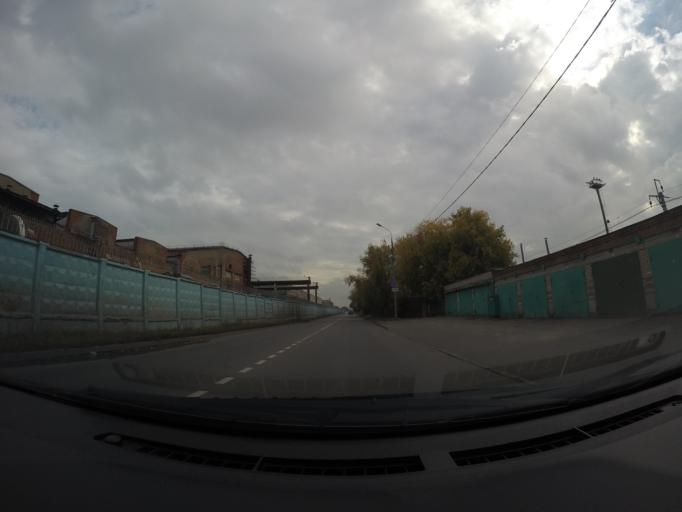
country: RU
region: Moscow
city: Lefortovo
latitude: 55.7695
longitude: 37.7199
